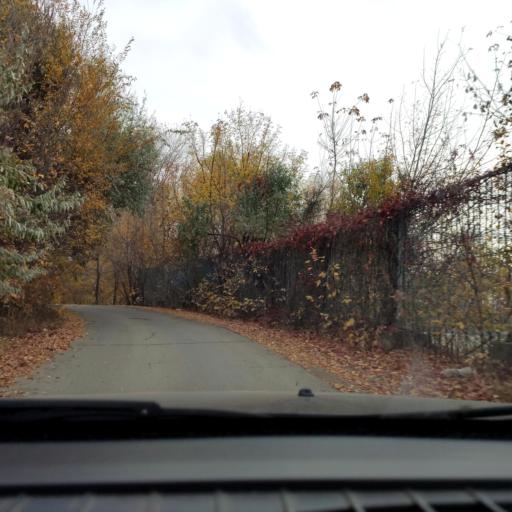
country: RU
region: Samara
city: Tol'yatti
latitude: 53.4978
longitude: 49.2626
